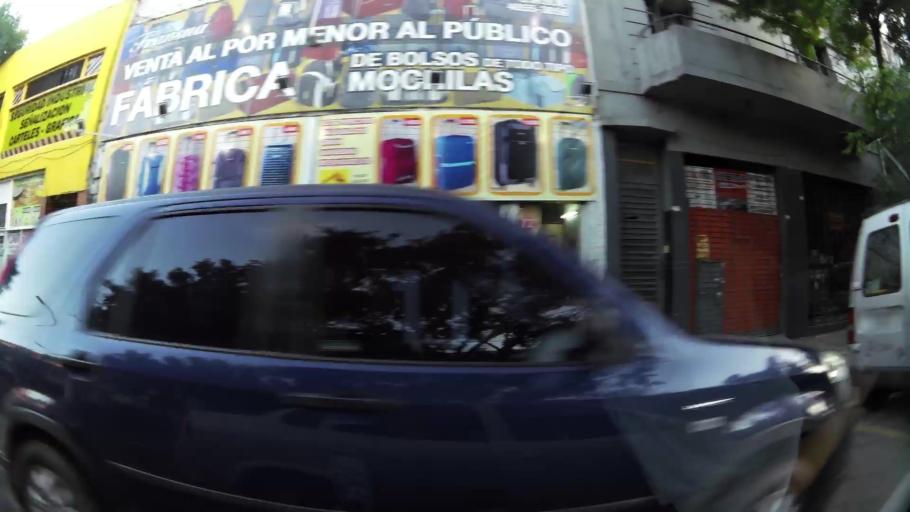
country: AR
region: Buenos Aires F.D.
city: Colegiales
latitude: -34.6021
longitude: -58.4437
